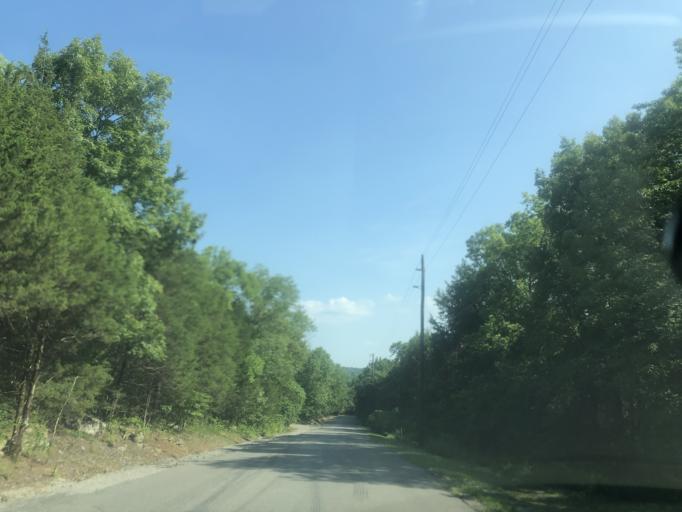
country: US
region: Tennessee
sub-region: Wilson County
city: Green Hill
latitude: 36.1351
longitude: -86.5944
